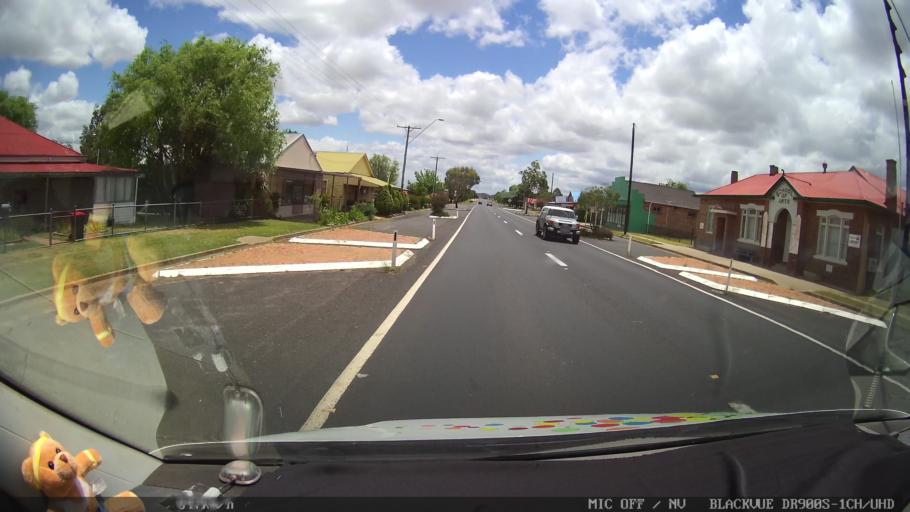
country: AU
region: New South Wales
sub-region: Glen Innes Severn
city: Glen Innes
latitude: -29.4407
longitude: 151.8464
